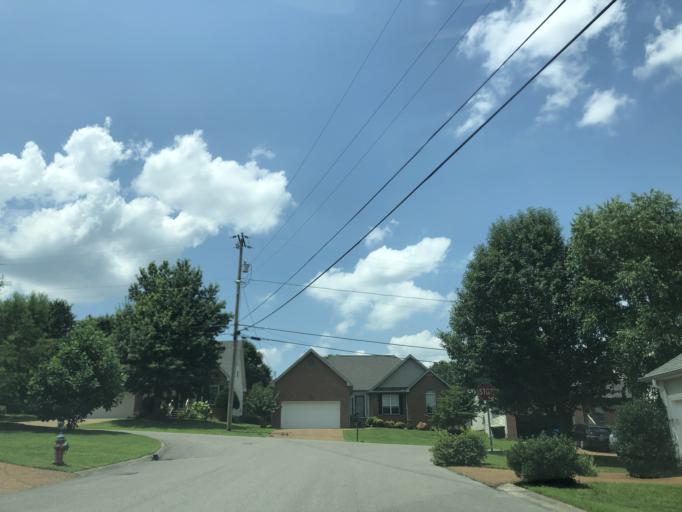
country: US
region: Tennessee
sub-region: Williamson County
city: Brentwood Estates
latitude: 36.0228
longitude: -86.7198
